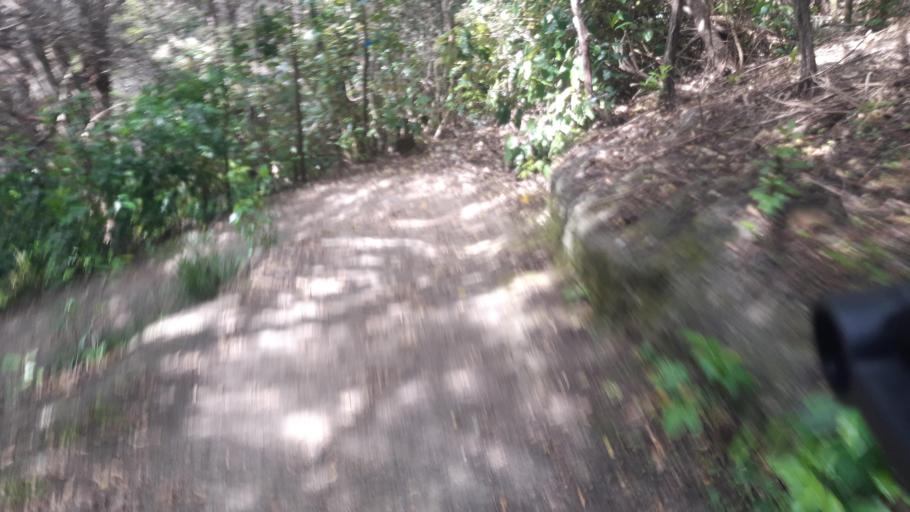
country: NZ
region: Marlborough
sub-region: Marlborough District
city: Picton
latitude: -41.2552
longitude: 174.0407
